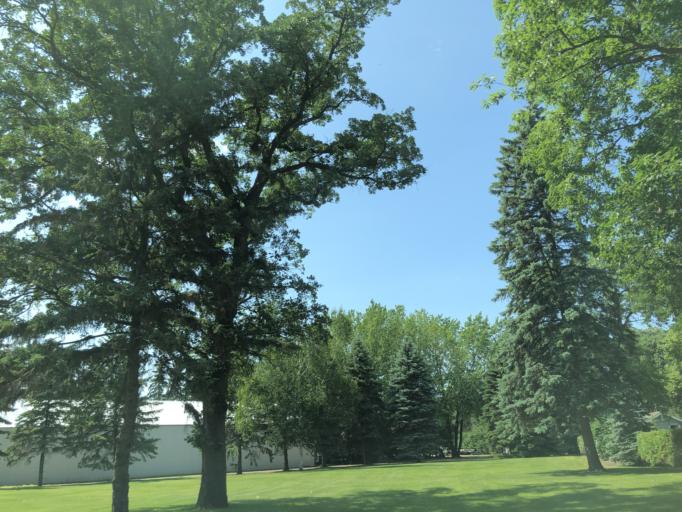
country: US
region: Minnesota
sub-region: Douglas County
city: Alexandria
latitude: 45.9395
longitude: -95.3786
